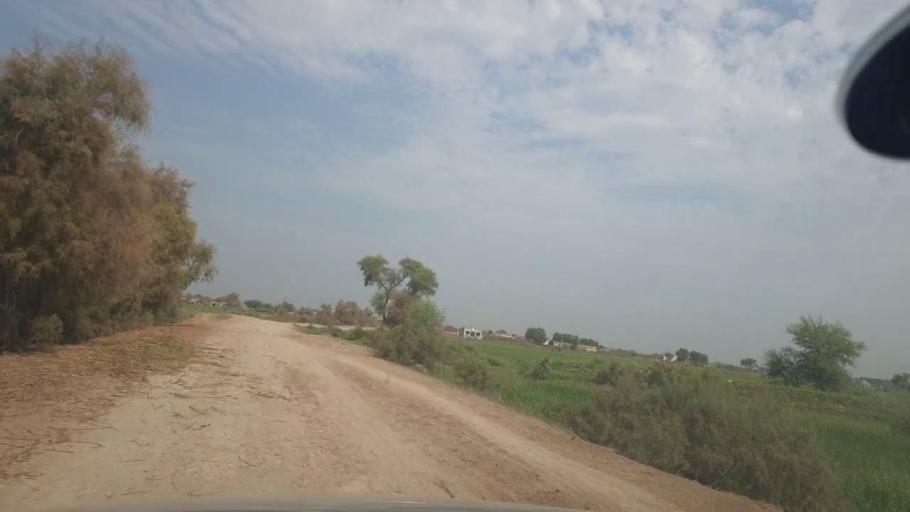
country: PK
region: Balochistan
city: Mehrabpur
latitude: 28.1256
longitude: 68.0896
